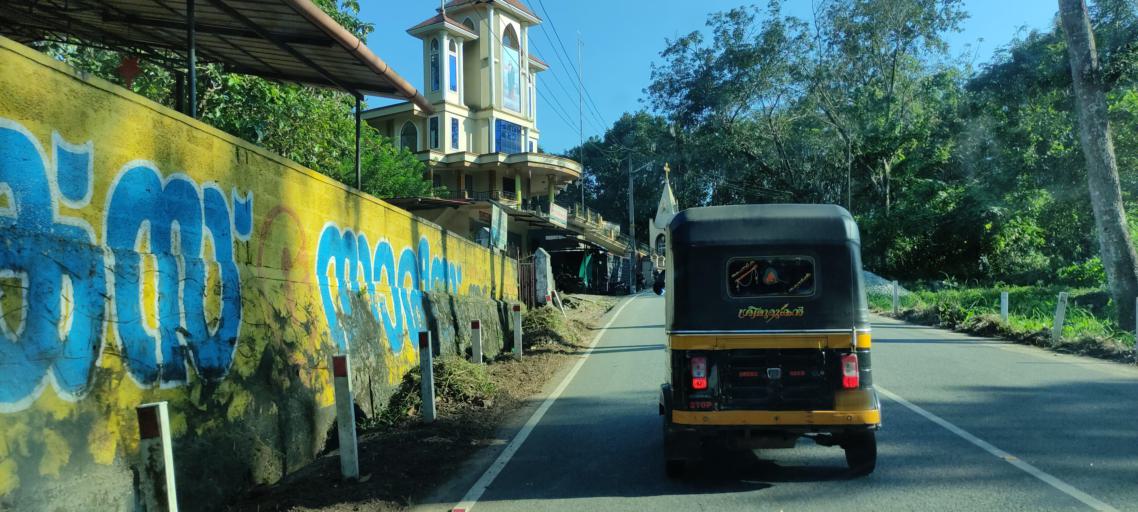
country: IN
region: Kerala
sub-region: Pattanamtitta
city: Adur
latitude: 9.1758
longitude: 76.7419
